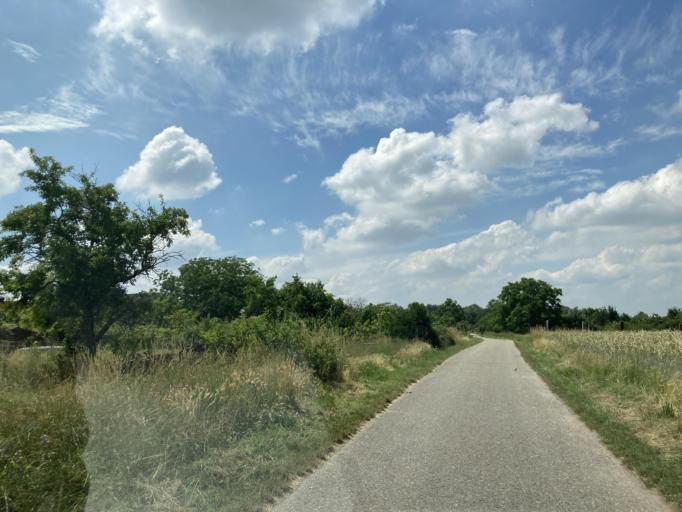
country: DE
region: Baden-Wuerttemberg
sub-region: Karlsruhe Region
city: Oberhausen-Rheinhausen
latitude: 49.2681
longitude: 8.4861
